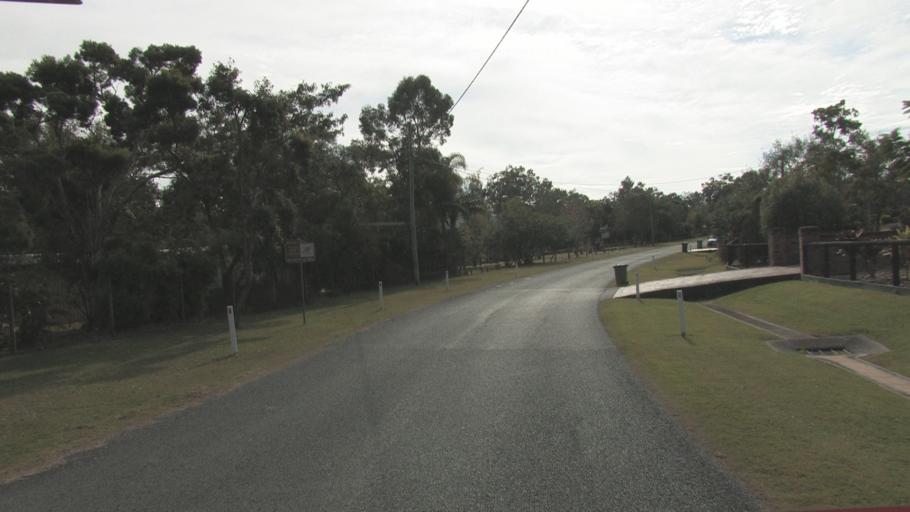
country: AU
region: Queensland
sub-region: Logan
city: Park Ridge South
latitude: -27.7400
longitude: 153.0384
